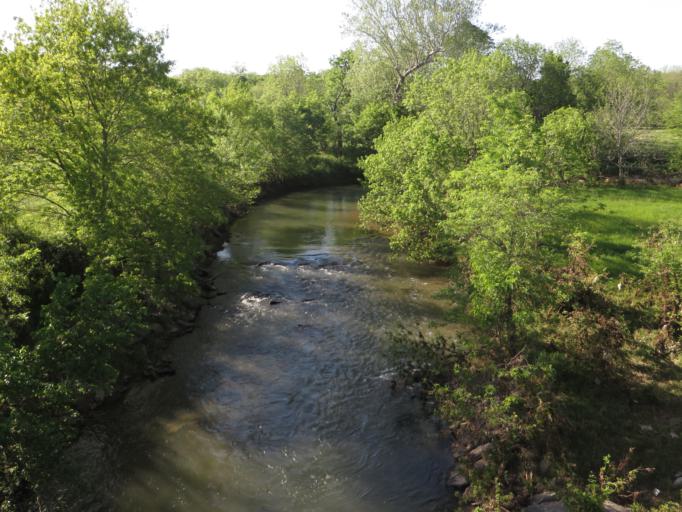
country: US
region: Missouri
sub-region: Greene County
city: Battlefield
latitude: 37.0917
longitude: -93.4043
